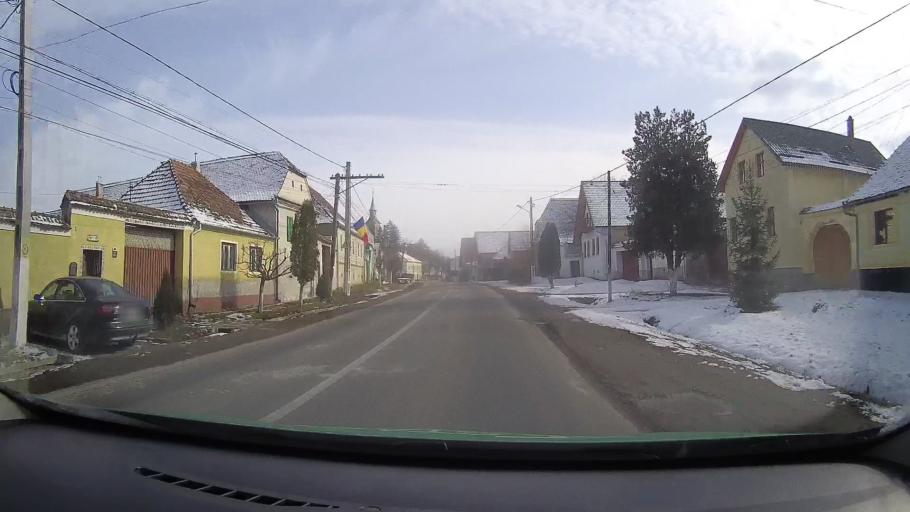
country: RO
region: Mures
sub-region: Comuna Apold
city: Saes
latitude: 46.1575
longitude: 24.7669
